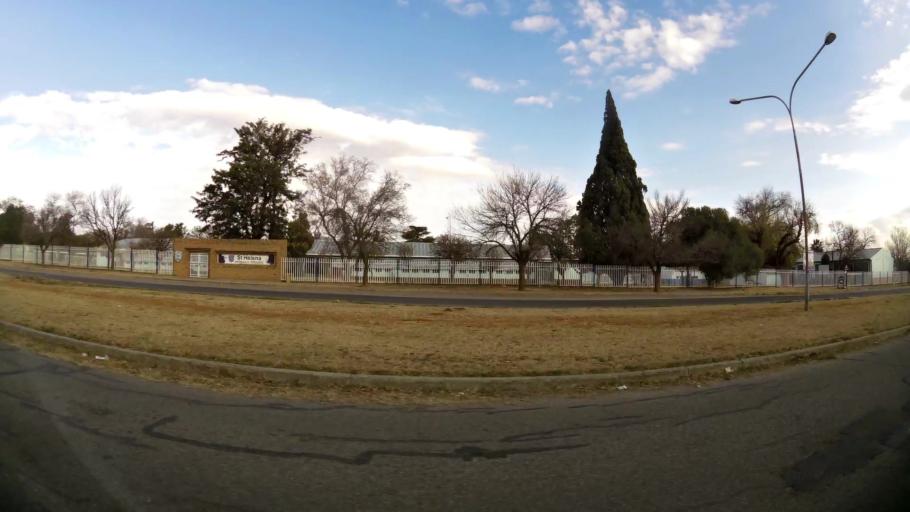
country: ZA
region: Orange Free State
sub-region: Lejweleputswa District Municipality
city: Welkom
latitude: -27.9891
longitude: 26.7173
